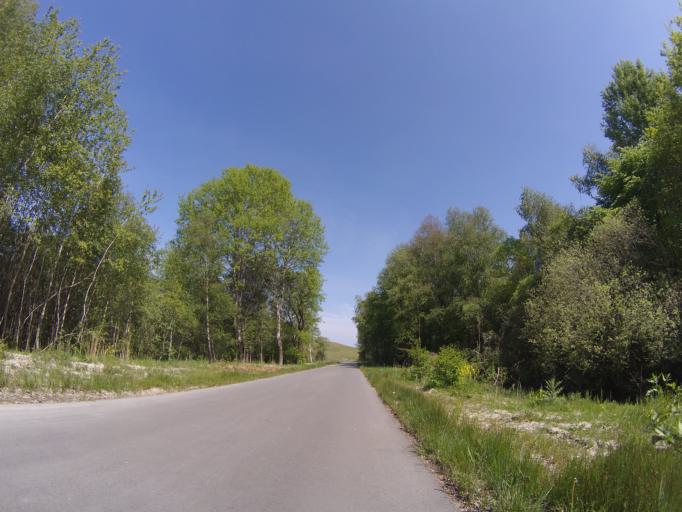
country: NL
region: Drenthe
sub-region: Gemeente Hoogeveen
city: Hoogeveen
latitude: 52.7803
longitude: 6.5187
